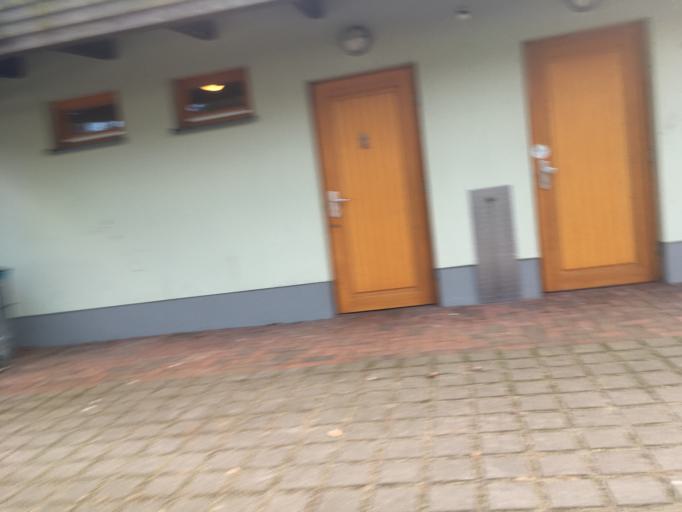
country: DE
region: Mecklenburg-Vorpommern
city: Ostseebad Sellin
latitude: 54.3630
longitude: 13.7140
